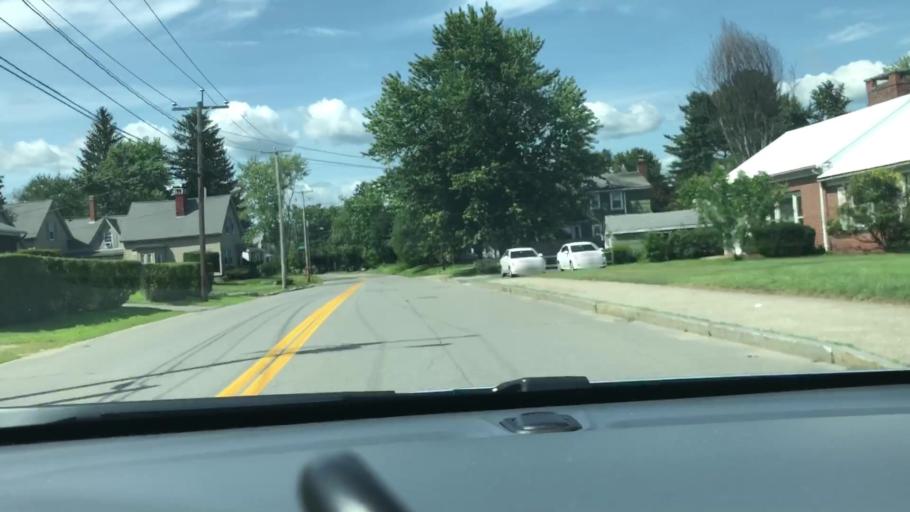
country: US
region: New Hampshire
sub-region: Hillsborough County
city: Pinardville
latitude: 42.9825
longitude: -71.4937
